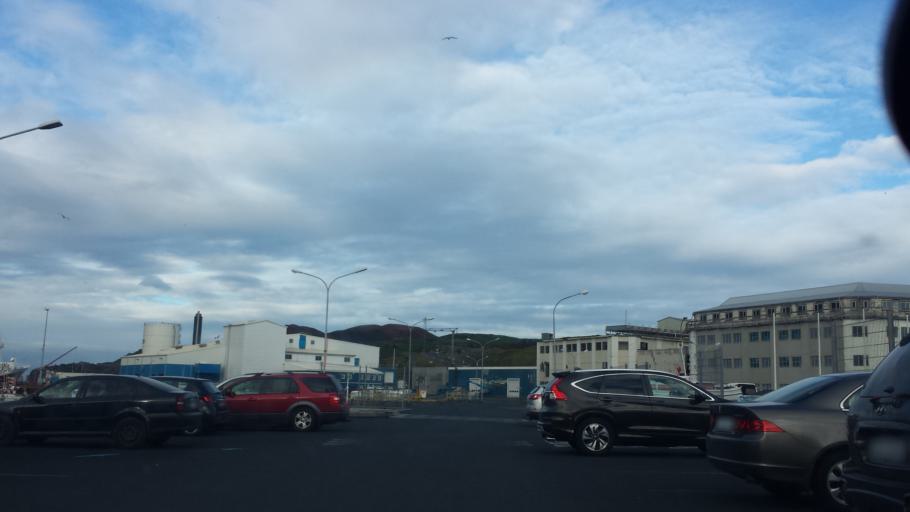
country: IS
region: South
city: Vestmannaeyjar
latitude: 63.4434
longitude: -20.2715
